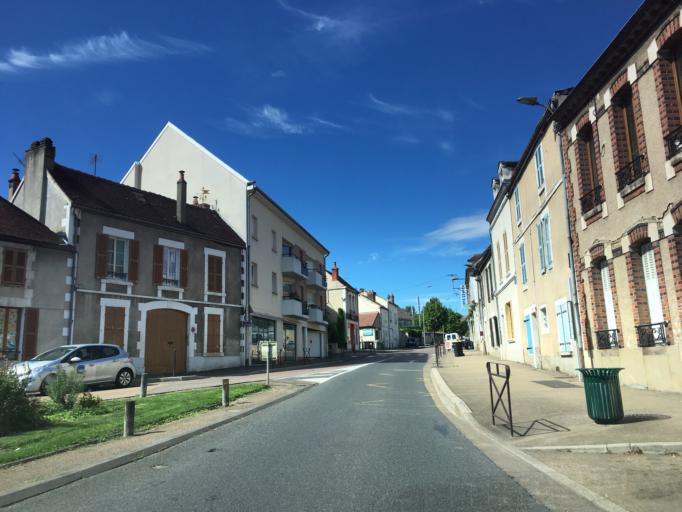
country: FR
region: Bourgogne
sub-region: Departement de l'Yonne
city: Auxerre
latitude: 47.7900
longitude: 3.5648
